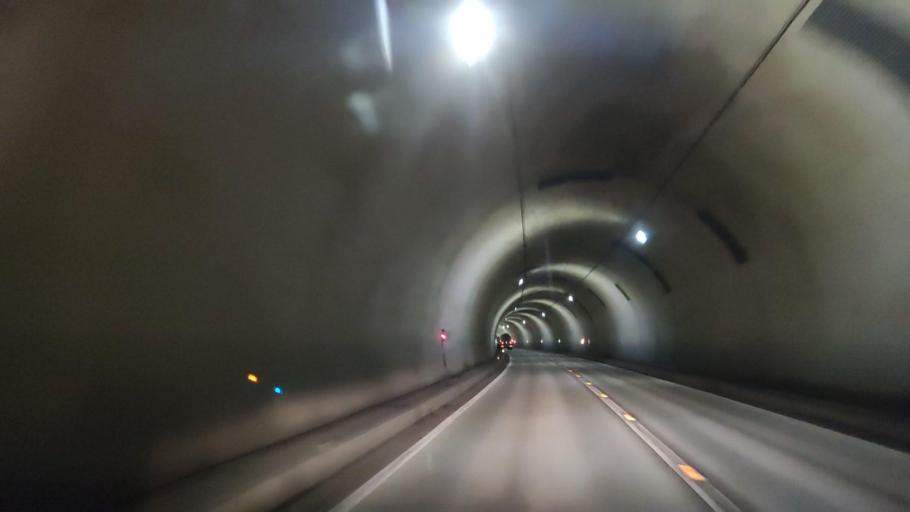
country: JP
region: Tottori
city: Yonago
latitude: 35.2636
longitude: 133.4358
